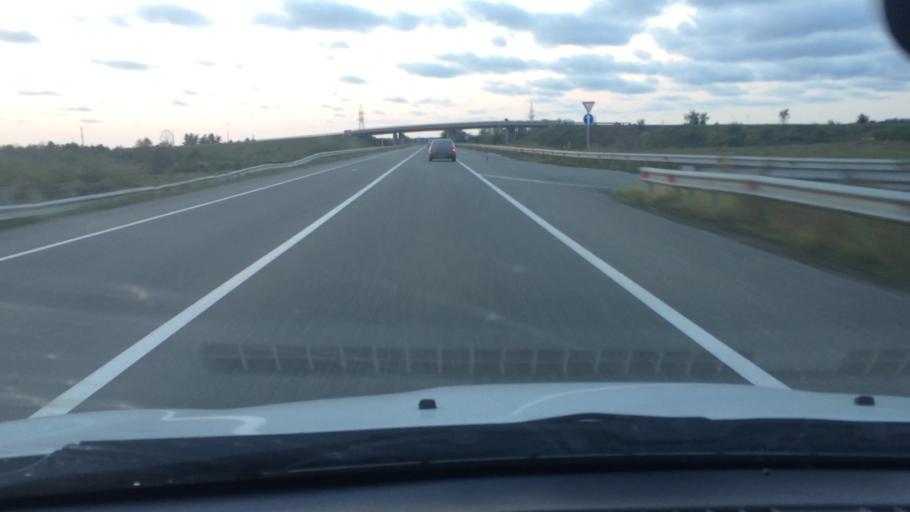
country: GE
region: Ajaria
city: Ochkhamuri
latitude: 41.8966
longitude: 41.7997
